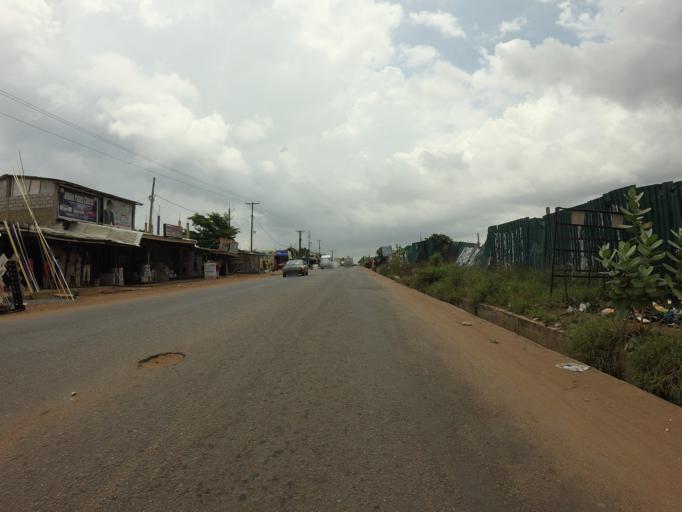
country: GH
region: Greater Accra
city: Medina Estates
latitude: 5.6862
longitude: -0.1582
